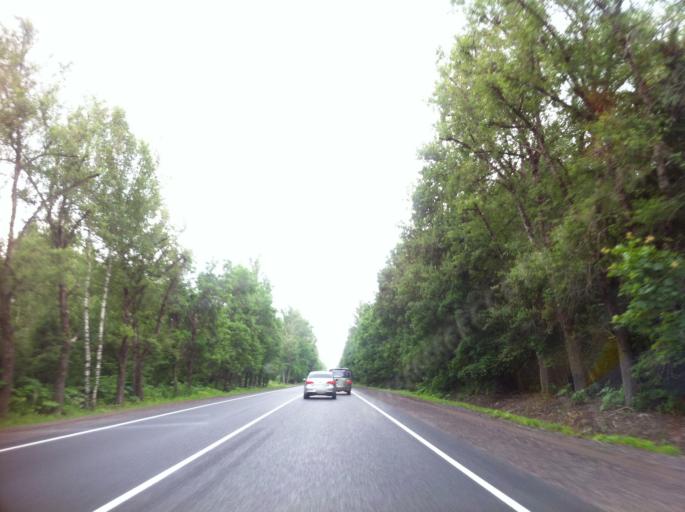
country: RU
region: Leningrad
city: Rozhdestveno
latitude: 59.1789
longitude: 29.9178
